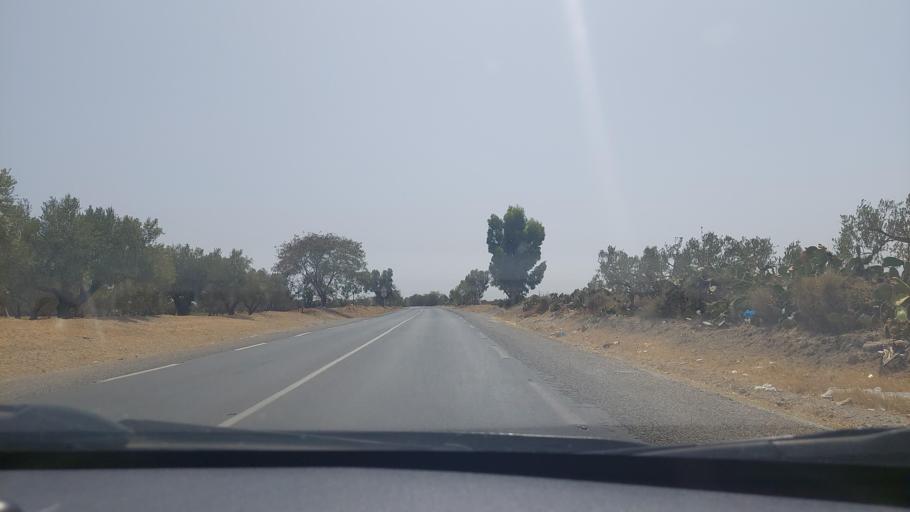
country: TN
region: Al Munastir
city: Sidi Bin Nur
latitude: 35.5719
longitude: 10.9104
